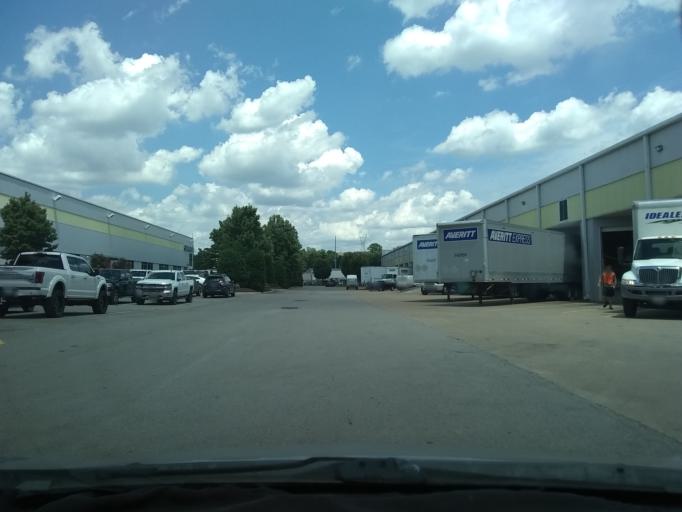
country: US
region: Tennessee
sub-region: Davidson County
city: Nashville
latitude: 36.1458
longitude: -86.7104
